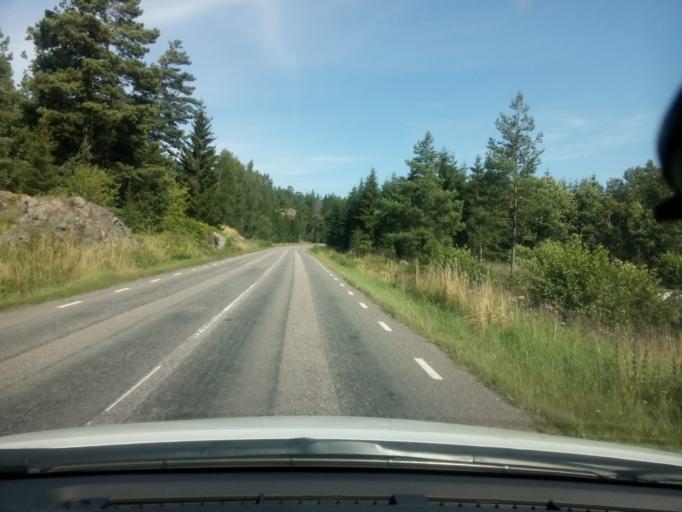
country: SE
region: Soedermanland
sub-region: Trosa Kommun
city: Trosa
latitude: 58.7989
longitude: 17.3344
